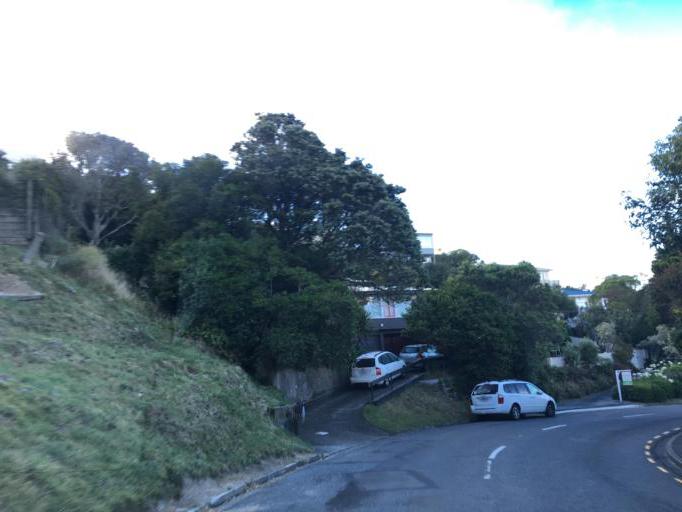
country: NZ
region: Wellington
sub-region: Wellington City
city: Kelburn
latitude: -41.2532
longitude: 174.7769
